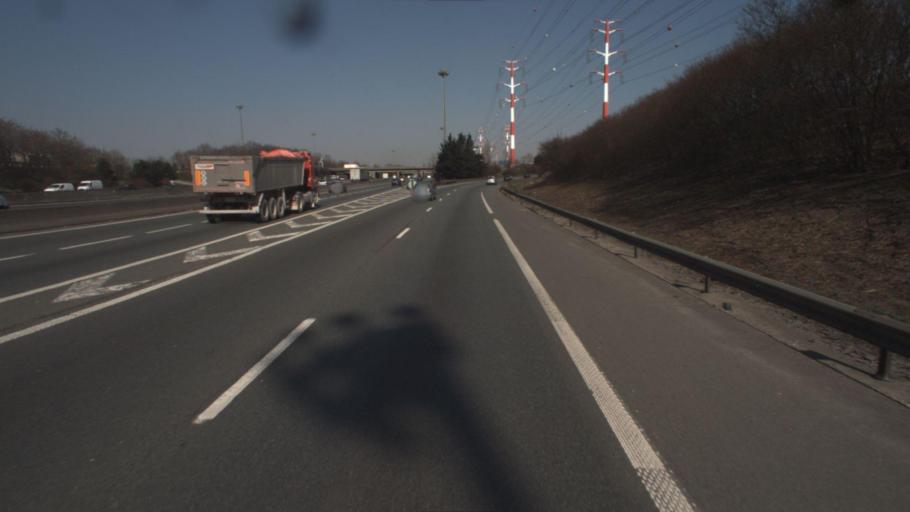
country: FR
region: Ile-de-France
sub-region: Departement du Val-de-Marne
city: Fresnes
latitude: 48.7533
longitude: 2.3322
